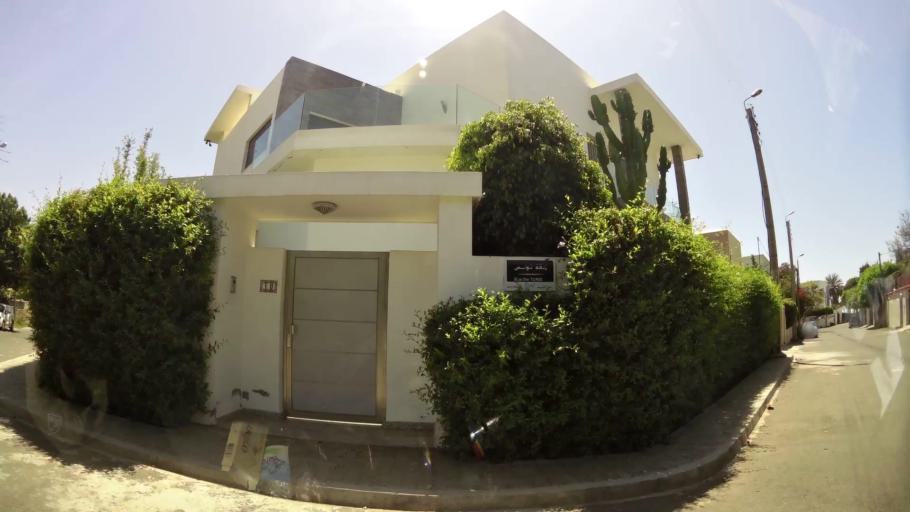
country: MA
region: Souss-Massa-Draa
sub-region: Agadir-Ida-ou-Tnan
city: Agadir
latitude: 30.4309
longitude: -9.5941
